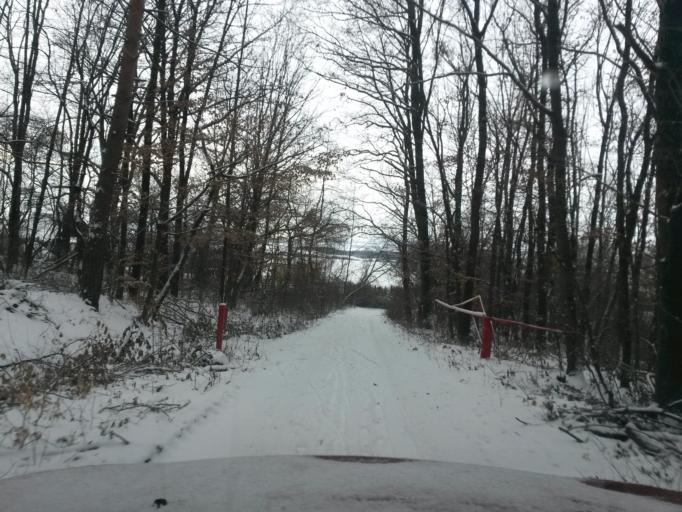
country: HU
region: Borsod-Abauj-Zemplen
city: Gonc
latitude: 48.6005
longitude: 21.3909
